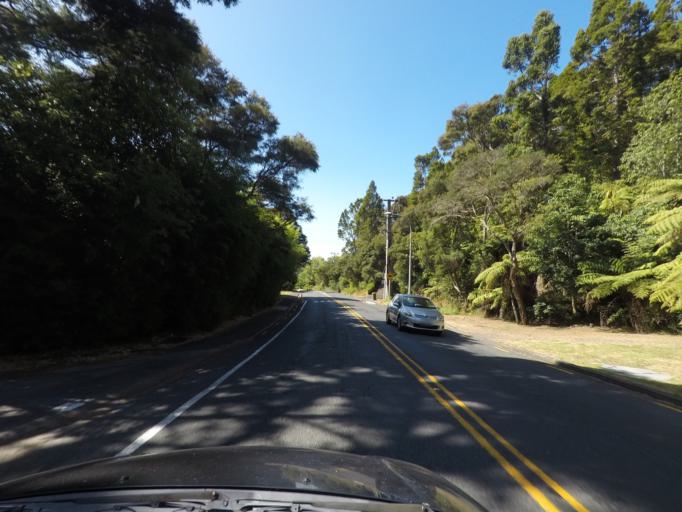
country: NZ
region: Auckland
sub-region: Auckland
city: Titirangi
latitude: -36.9368
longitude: 174.6547
